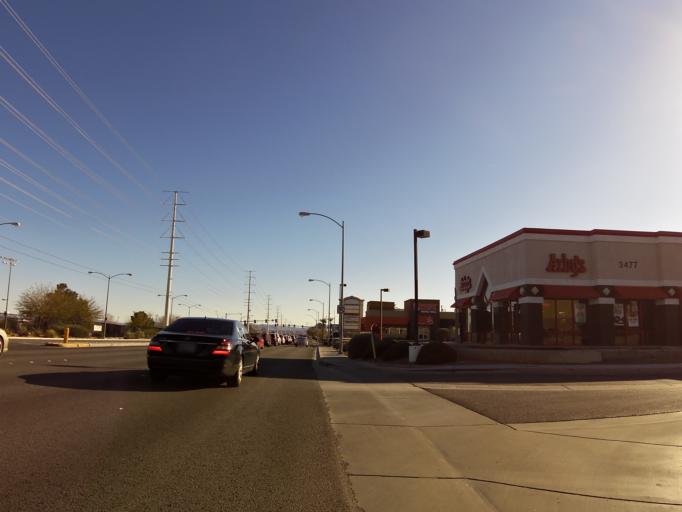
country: US
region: Nevada
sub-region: Clark County
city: Spring Valley
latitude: 36.1278
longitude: -115.2792
